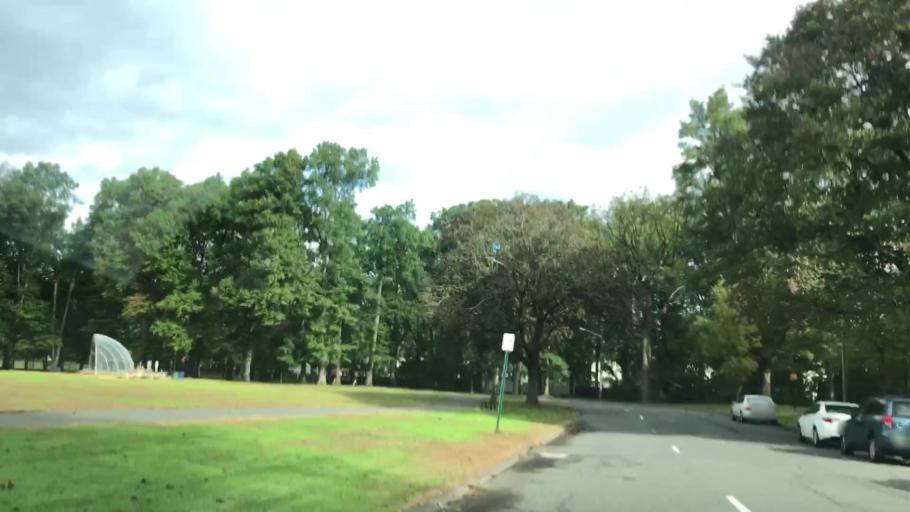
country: US
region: New Jersey
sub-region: Union County
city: Rahway
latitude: 40.6217
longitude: -74.2829
